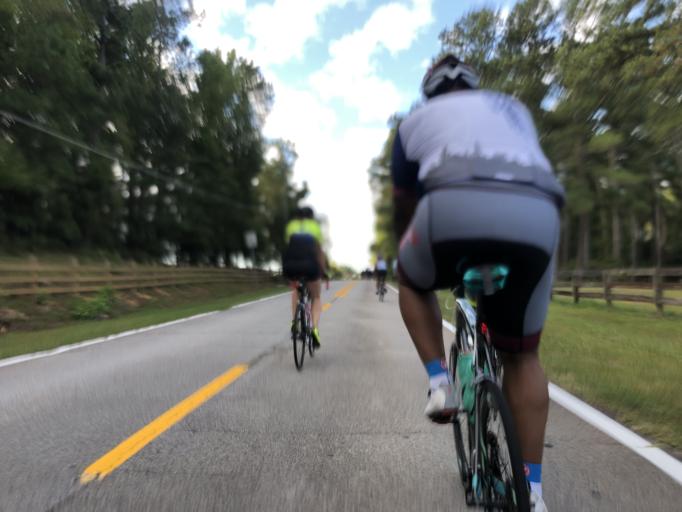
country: US
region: Georgia
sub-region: Fulton County
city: Palmetto
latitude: 33.5740
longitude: -84.6499
